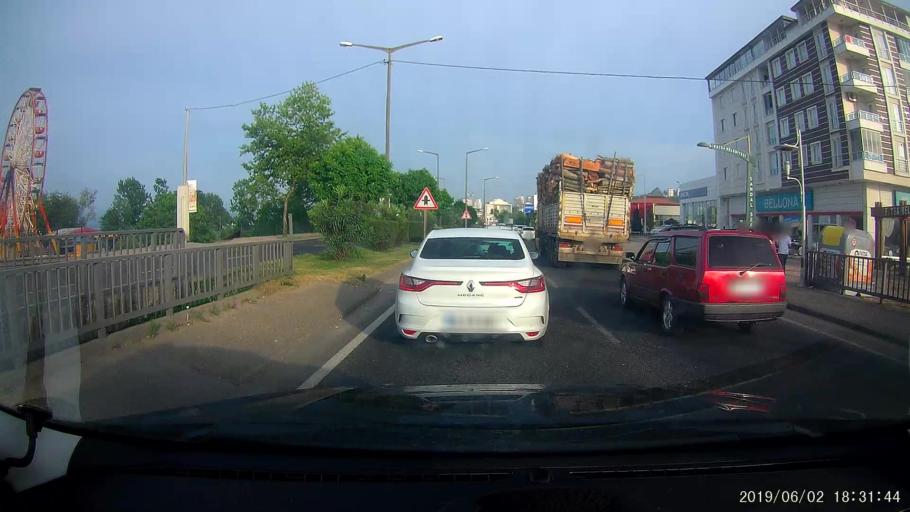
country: TR
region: Ordu
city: Fatsa
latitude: 41.0368
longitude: 37.4929
